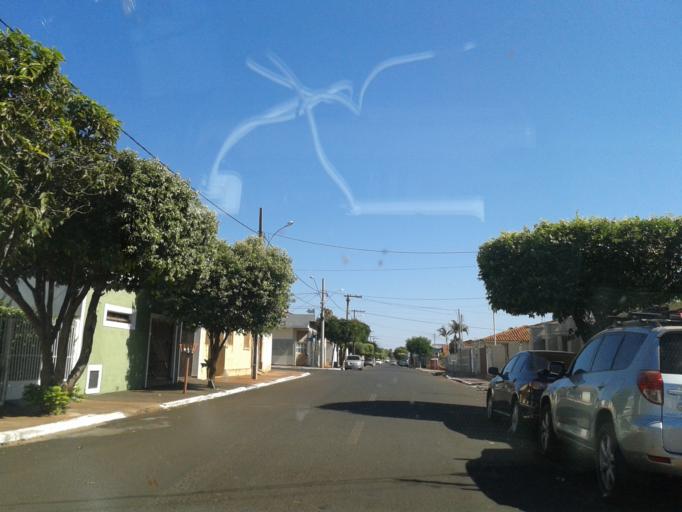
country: BR
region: Minas Gerais
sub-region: Santa Vitoria
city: Santa Vitoria
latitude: -18.8422
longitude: -50.1260
